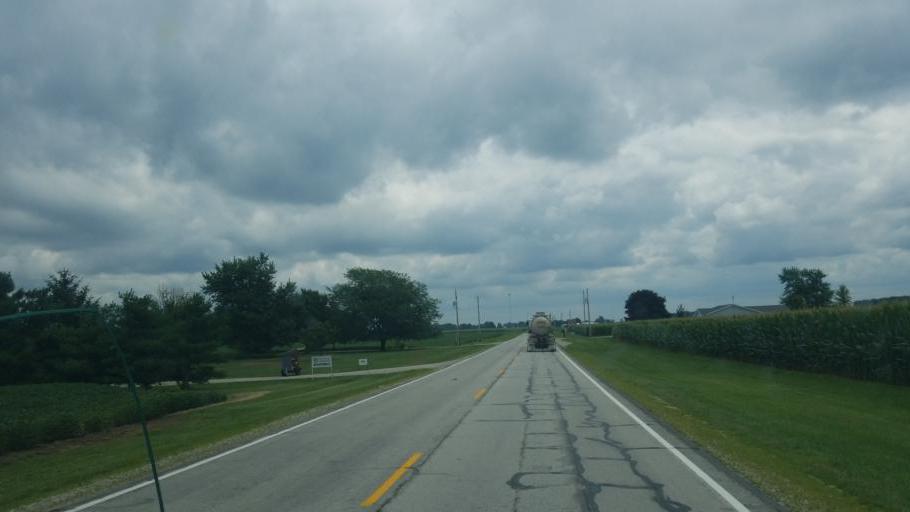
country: US
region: Indiana
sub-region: Wells County
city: Bluffton
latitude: 40.6549
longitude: -85.1724
